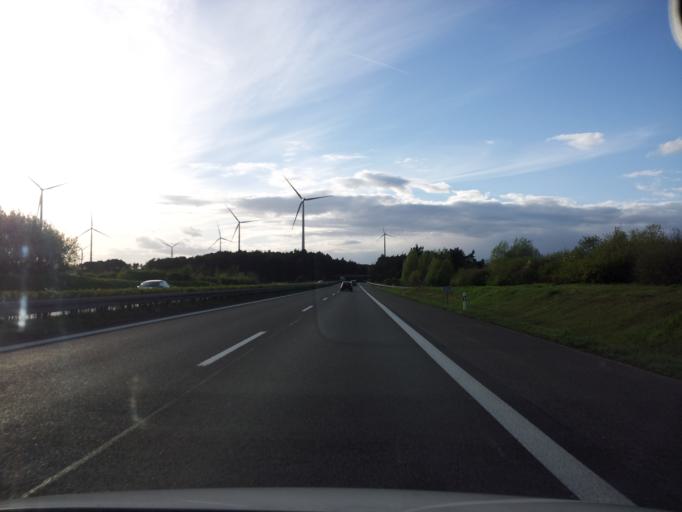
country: DE
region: Brandenburg
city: Vetschau
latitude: 51.7549
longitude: 14.1268
